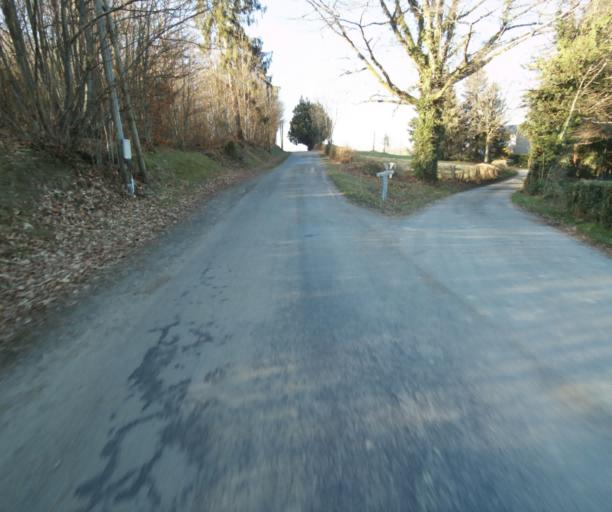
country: FR
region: Limousin
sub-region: Departement de la Correze
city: Uzerche
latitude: 45.3872
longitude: 1.5887
